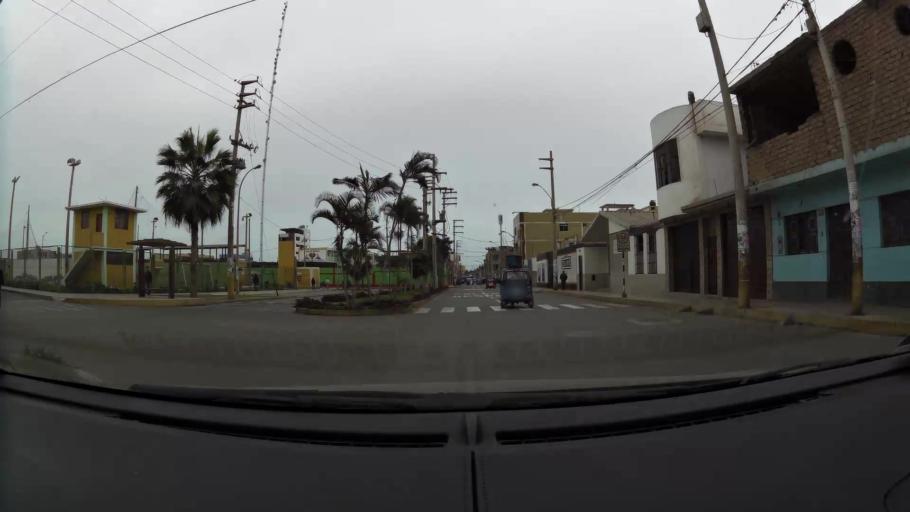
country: PE
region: Lima
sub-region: Barranca
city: Barranca
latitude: -10.7506
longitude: -77.7569
